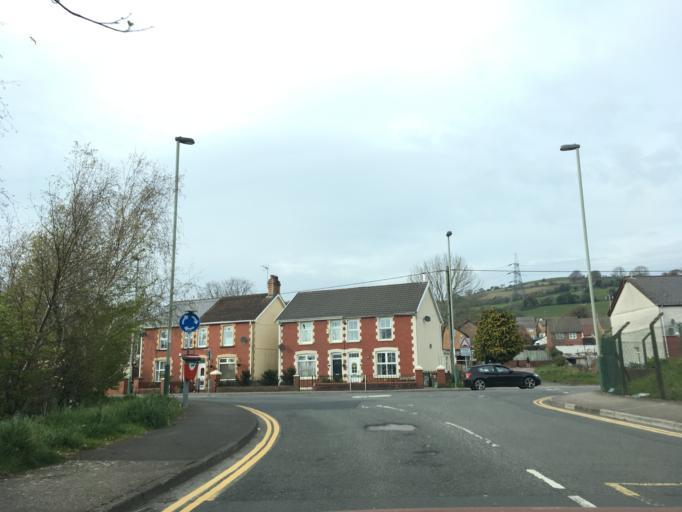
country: GB
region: Wales
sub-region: Caerphilly County Borough
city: Bedwas
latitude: 51.5937
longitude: -3.2104
